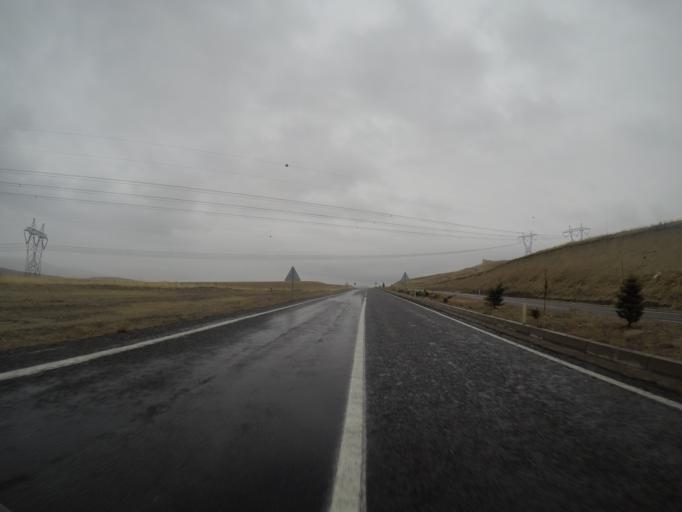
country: TR
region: Nevsehir
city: Avanos
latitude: 38.7080
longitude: 34.8781
